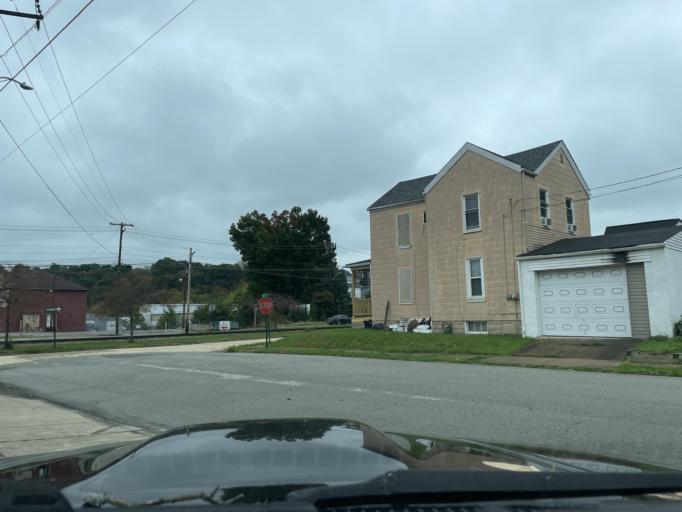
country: US
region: Pennsylvania
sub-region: Westmoreland County
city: New Kensington
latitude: 40.5613
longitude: -79.7635
